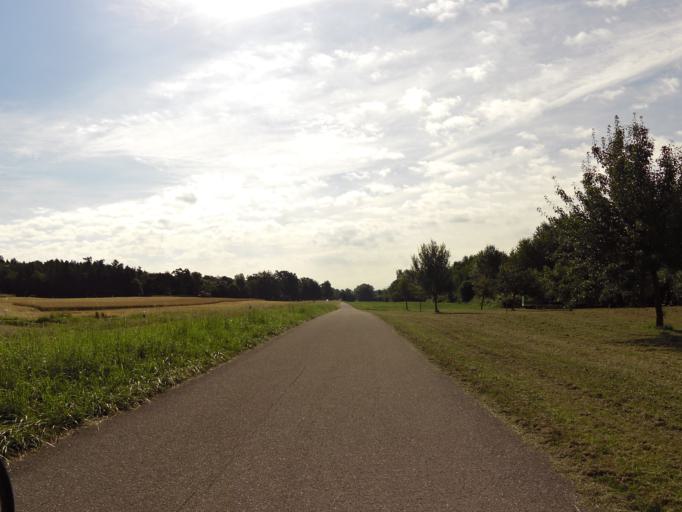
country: DE
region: Baden-Wuerttemberg
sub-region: Freiburg Region
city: Radolfzell am Bodensee
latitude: 47.7329
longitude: 9.0170
